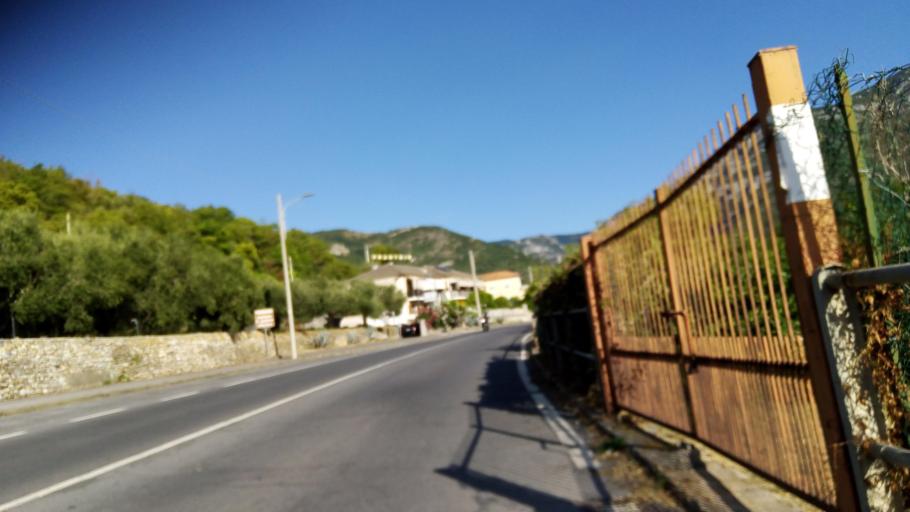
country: IT
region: Liguria
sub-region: Provincia di Savona
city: Toirano
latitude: 44.1220
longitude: 8.2152
